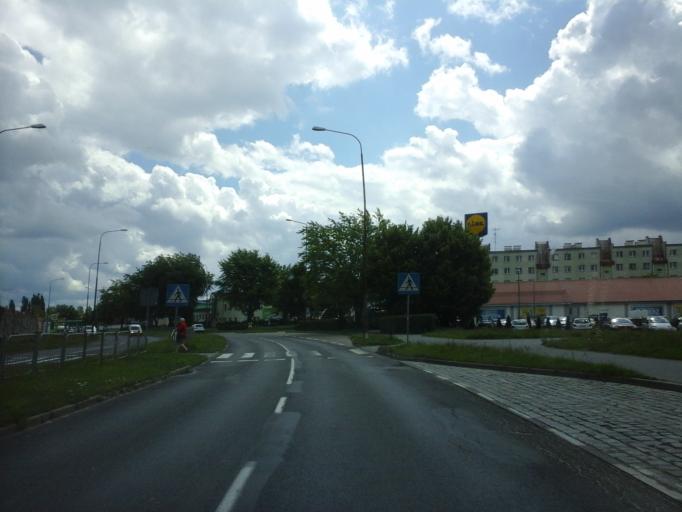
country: PL
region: West Pomeranian Voivodeship
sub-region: Koszalin
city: Koszalin
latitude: 54.1838
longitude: 16.1789
